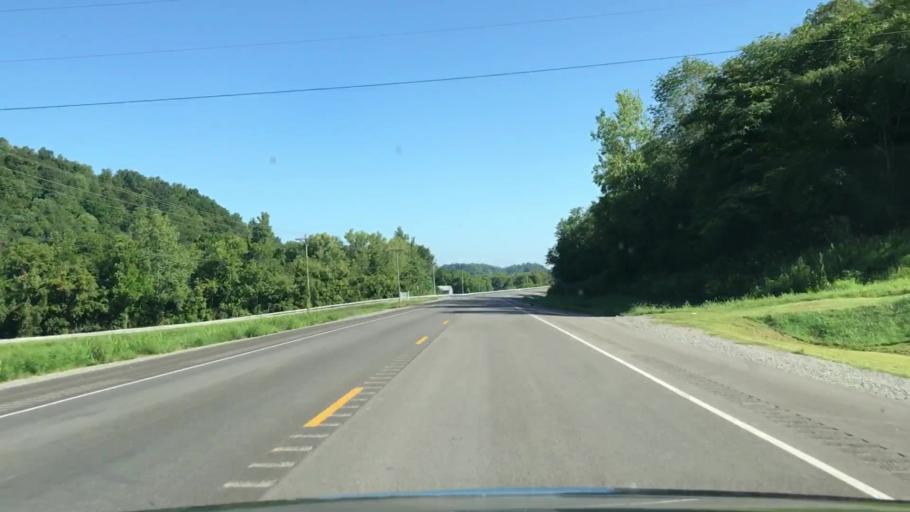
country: US
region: Kentucky
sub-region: Cumberland County
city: Burkesville
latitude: 36.7393
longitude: -85.3733
